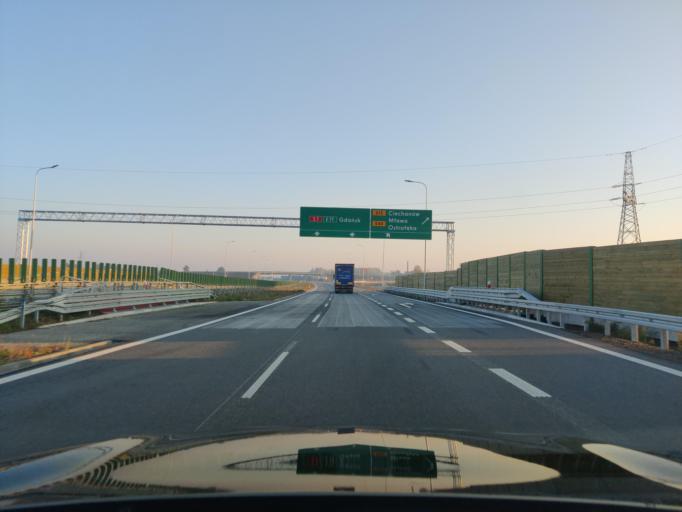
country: PL
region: Masovian Voivodeship
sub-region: Powiat mlawski
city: Mlawa
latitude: 53.0944
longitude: 20.4109
